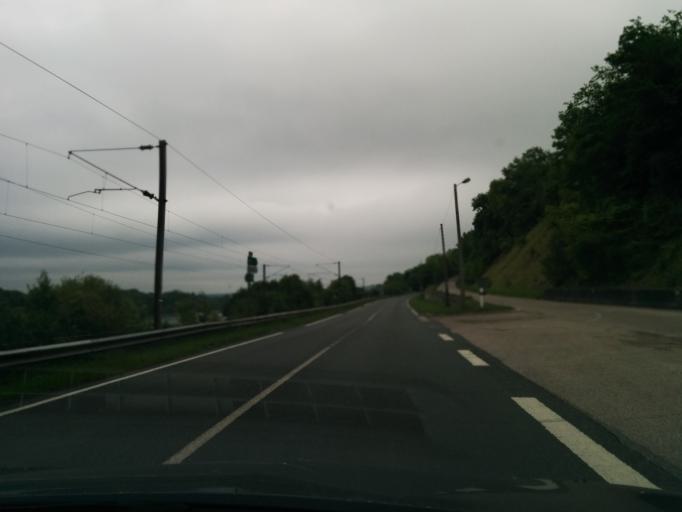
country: FR
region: Ile-de-France
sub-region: Departement des Yvelines
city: Limetz-Villez
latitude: 49.0680
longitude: 1.5188
